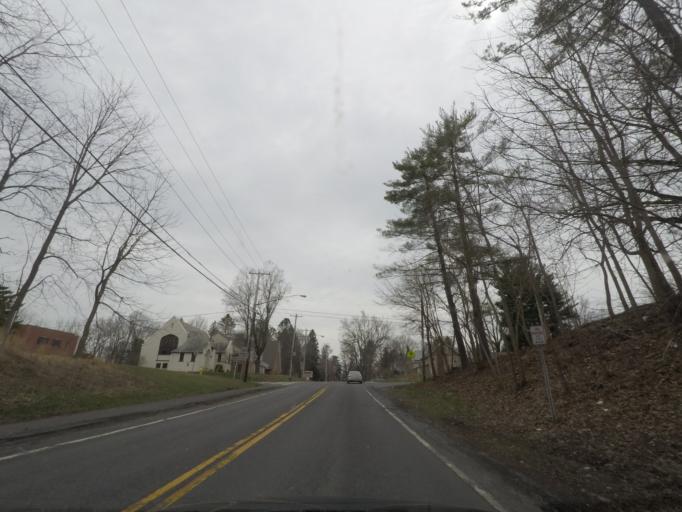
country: US
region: New York
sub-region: Albany County
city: Delmar
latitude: 42.6250
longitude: -73.8210
